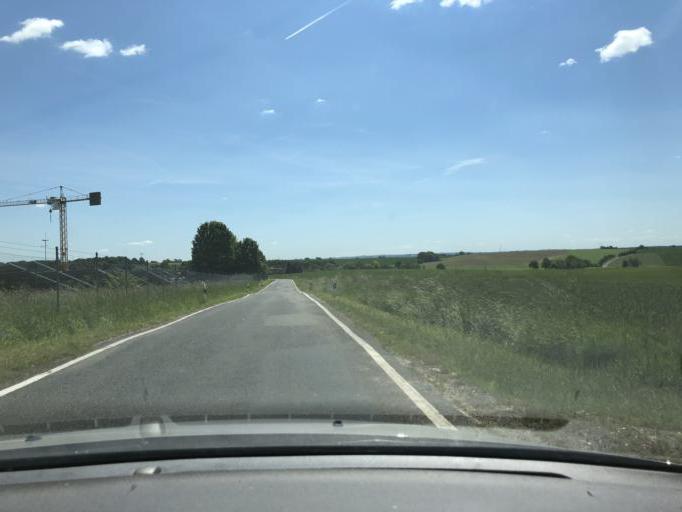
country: DE
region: Saxony
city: Nerchau
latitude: 51.2346
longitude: 12.8271
